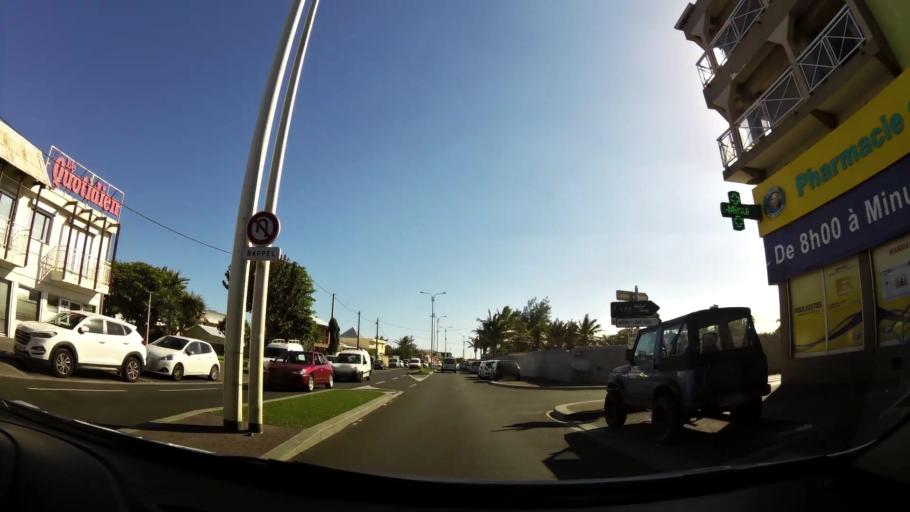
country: RE
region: Reunion
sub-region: Reunion
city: Saint-Pierre
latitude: -21.3435
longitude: 55.4695
